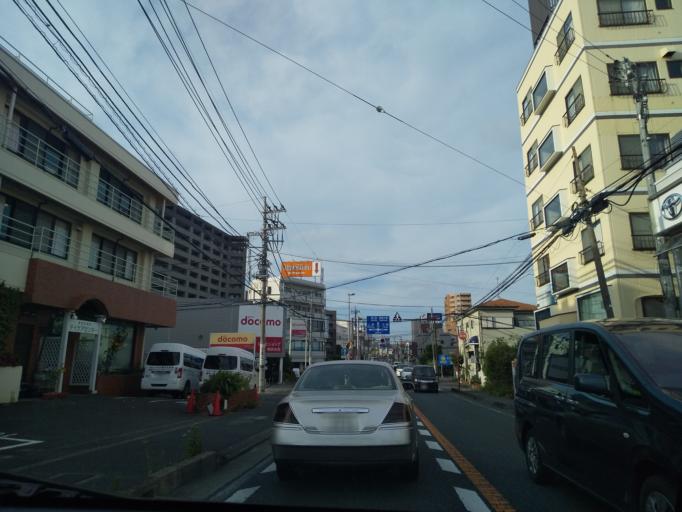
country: JP
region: Kanagawa
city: Zama
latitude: 35.5059
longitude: 139.4123
